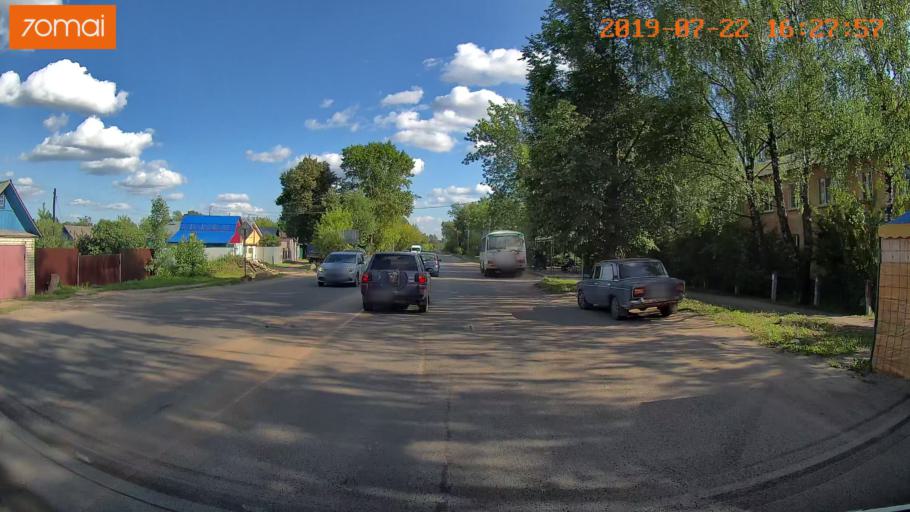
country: RU
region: Ivanovo
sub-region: Gorod Ivanovo
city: Ivanovo
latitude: 57.0415
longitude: 40.9477
